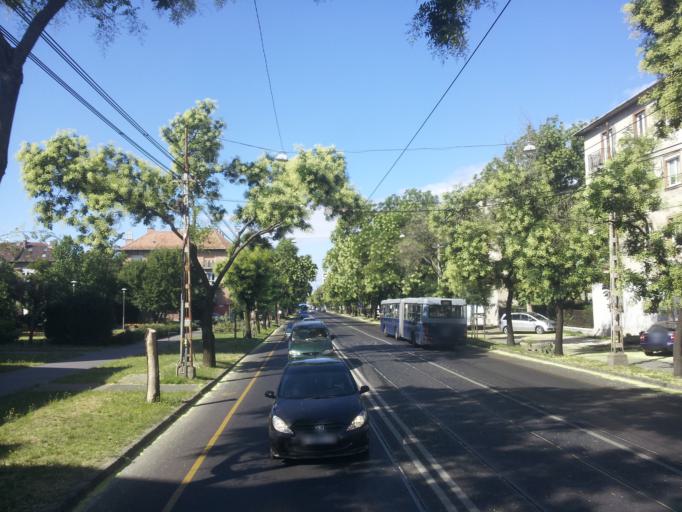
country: HU
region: Budapest
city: Budapest XIV. keruelet
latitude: 47.5159
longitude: 19.1065
